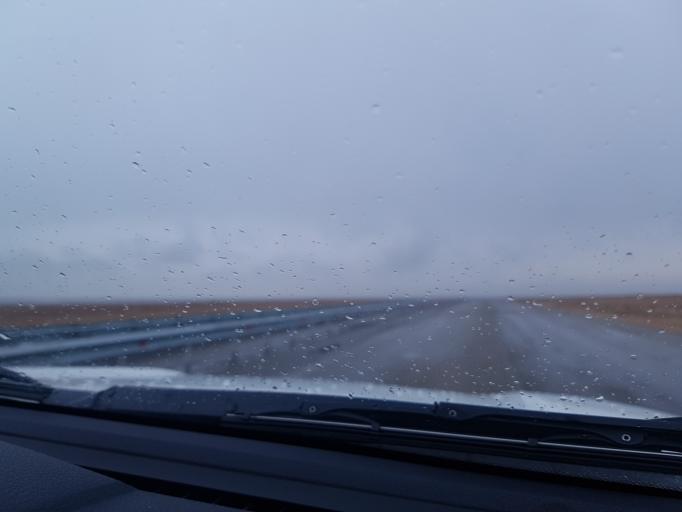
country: TM
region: Balkan
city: Turkmenbasy
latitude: 40.0042
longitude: 53.7154
